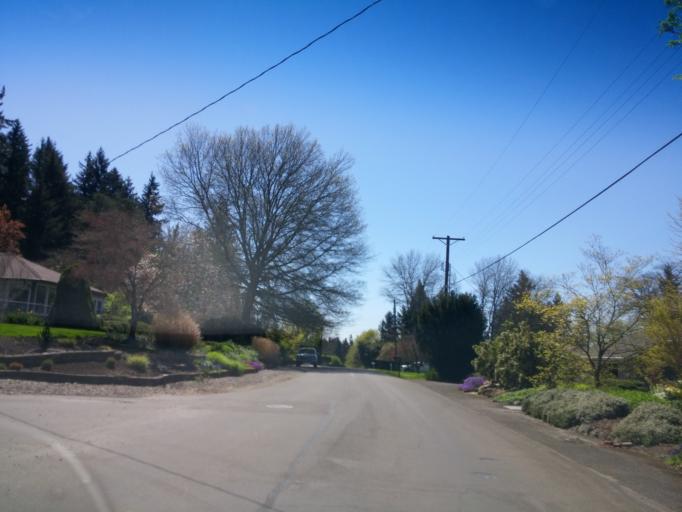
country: US
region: Oregon
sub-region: Washington County
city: West Haven
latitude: 45.5217
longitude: -122.7806
